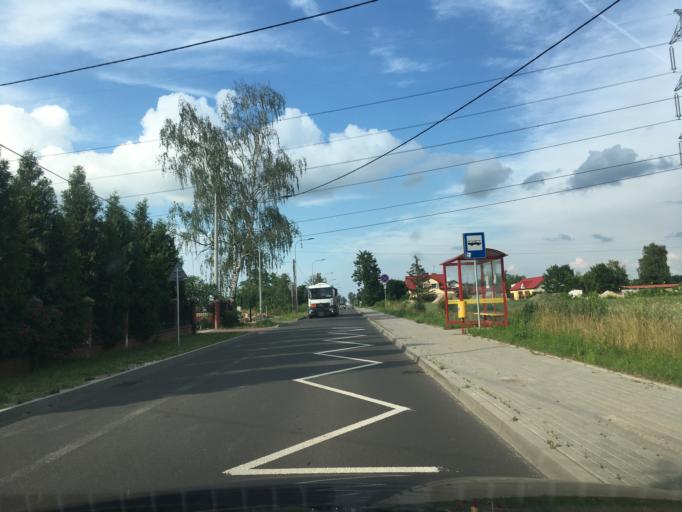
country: PL
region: Masovian Voivodeship
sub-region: Powiat wolominski
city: Radzymin
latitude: 52.4051
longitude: 21.2094
